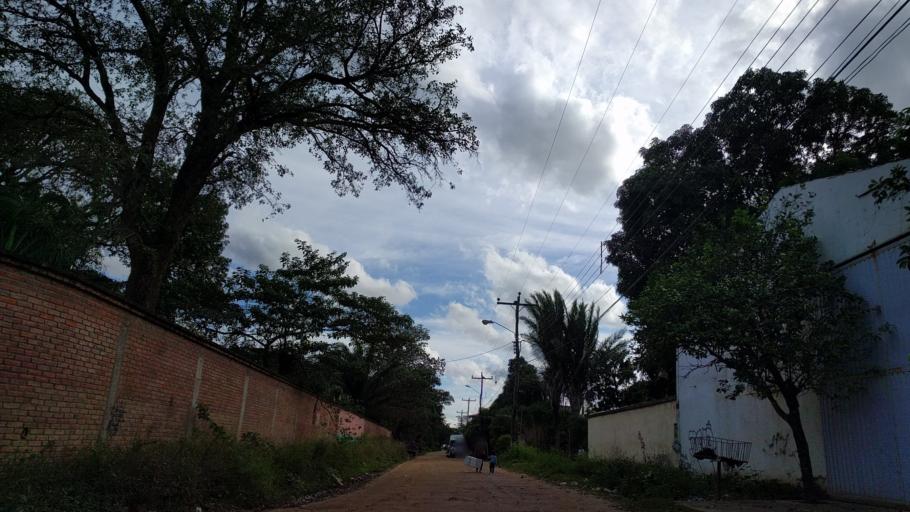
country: BO
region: Santa Cruz
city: Santa Cruz de la Sierra
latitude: -17.8495
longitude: -63.2525
